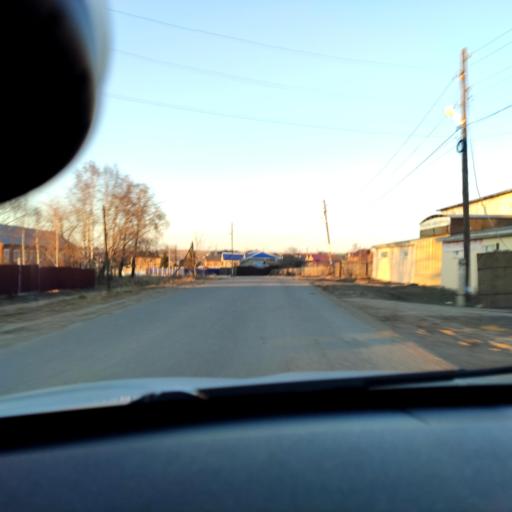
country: RU
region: Perm
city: Kultayevo
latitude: 57.9313
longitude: 55.8770
